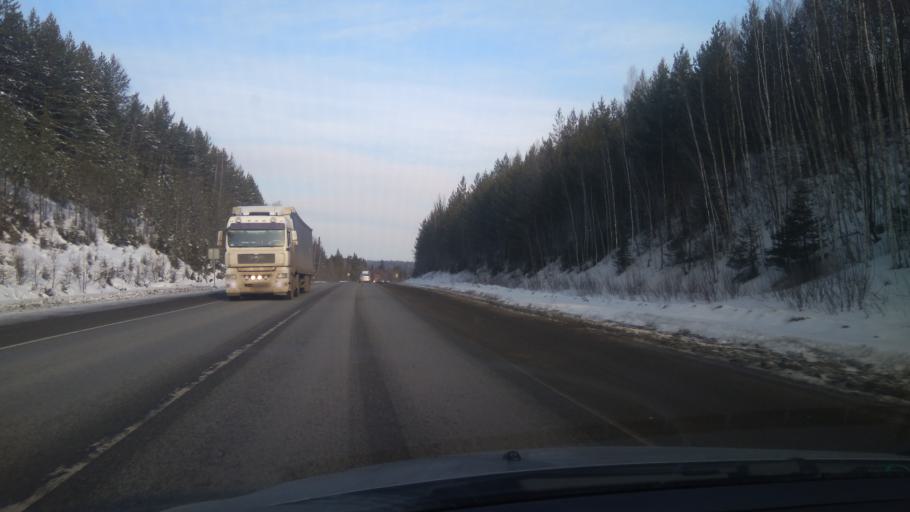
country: RU
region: Sverdlovsk
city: Revda
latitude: 56.8364
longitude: 59.8332
